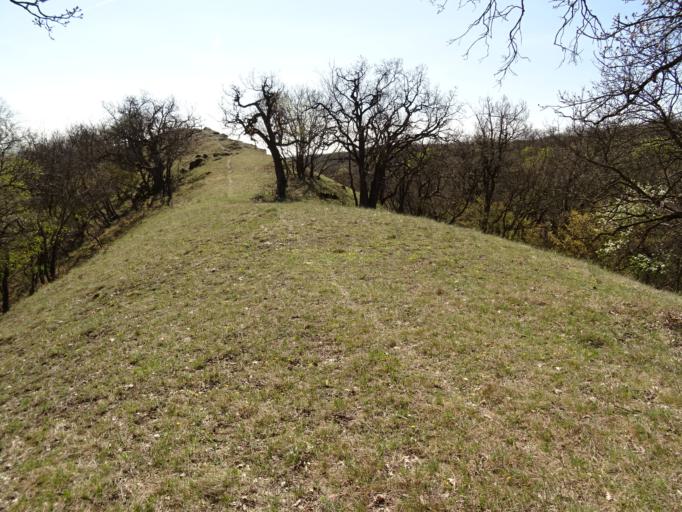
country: HU
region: Fejer
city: Csakvar
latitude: 47.4323
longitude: 18.4378
